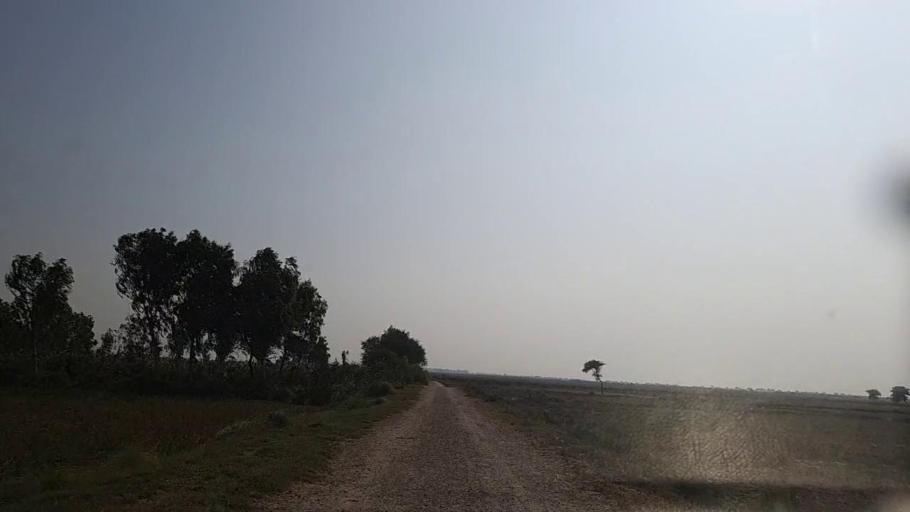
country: PK
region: Sindh
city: Mirpur Batoro
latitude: 24.5681
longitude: 68.2197
